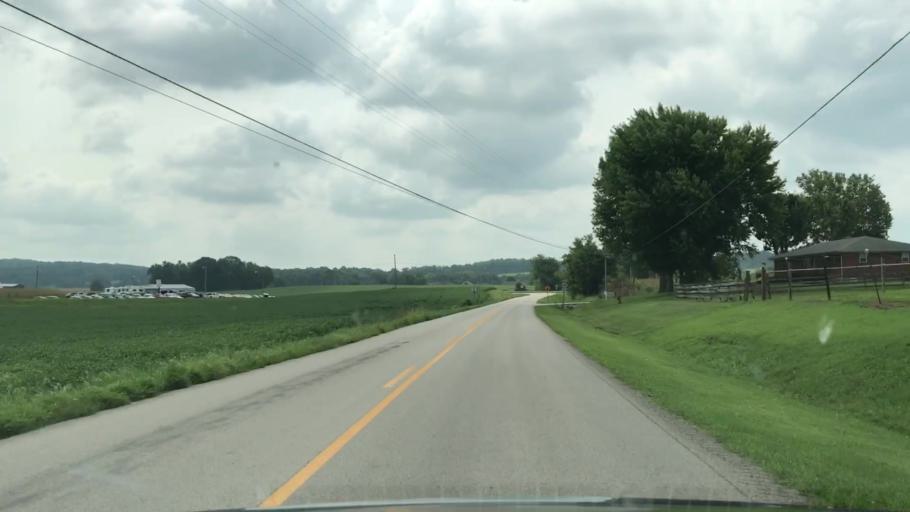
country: US
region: Kentucky
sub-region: Barren County
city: Cave City
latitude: 37.0987
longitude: -85.9753
